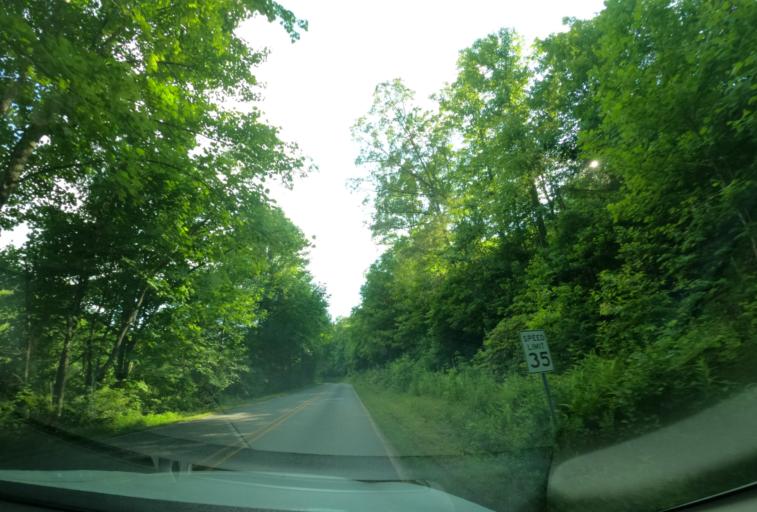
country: US
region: North Carolina
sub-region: Transylvania County
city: Brevard
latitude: 35.2447
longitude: -82.8572
